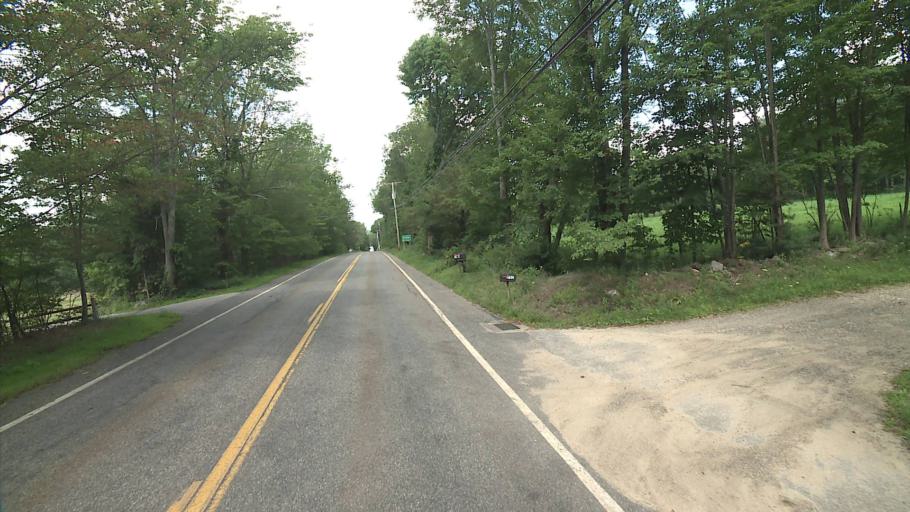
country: US
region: Connecticut
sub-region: Tolland County
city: Storrs
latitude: 41.9148
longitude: -72.1740
